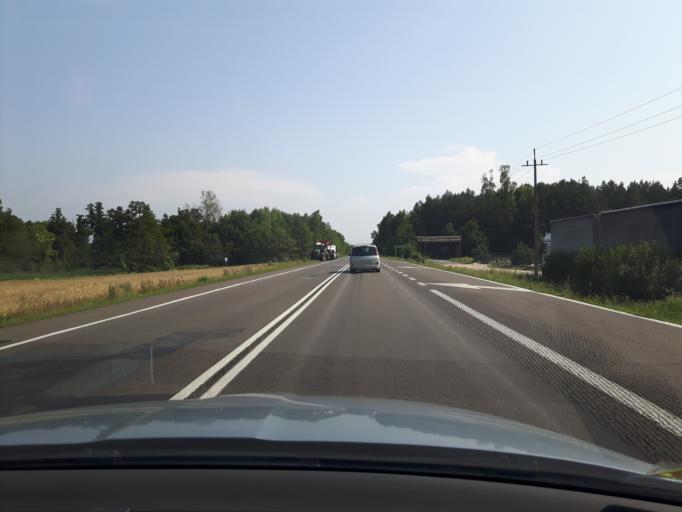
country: PL
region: Masovian Voivodeship
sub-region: Powiat ciechanowski
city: Glinojeck
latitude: 52.8175
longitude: 20.2646
